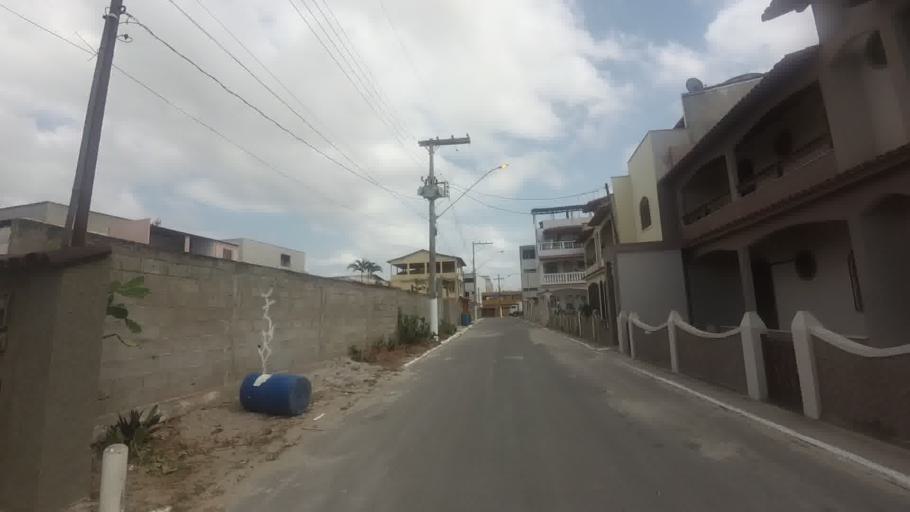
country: BR
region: Espirito Santo
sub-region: Piuma
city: Piuma
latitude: -20.8955
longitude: -40.7757
